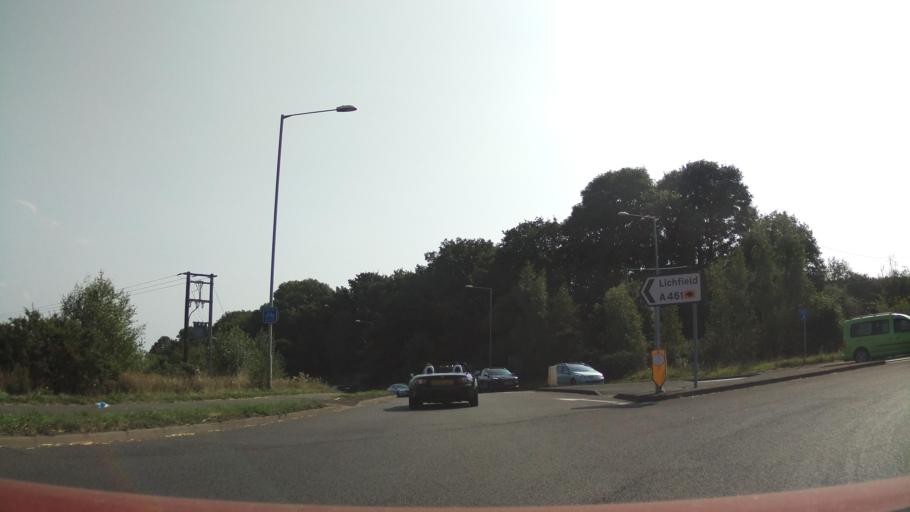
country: GB
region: England
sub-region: Staffordshire
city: Lichfield
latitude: 52.6735
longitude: -1.8599
